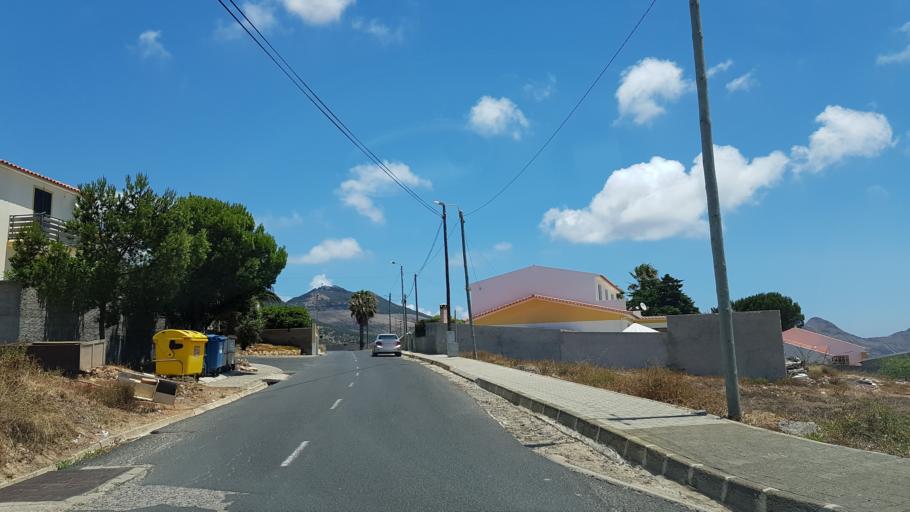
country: PT
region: Madeira
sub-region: Porto Santo
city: Vila de Porto Santo
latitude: 33.0608
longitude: -16.3538
